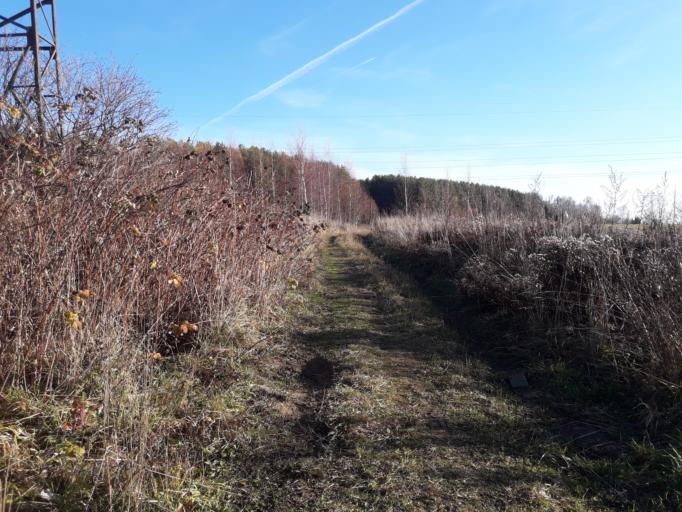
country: RU
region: Moskovskaya
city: Ashukino
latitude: 56.1623
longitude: 37.9662
